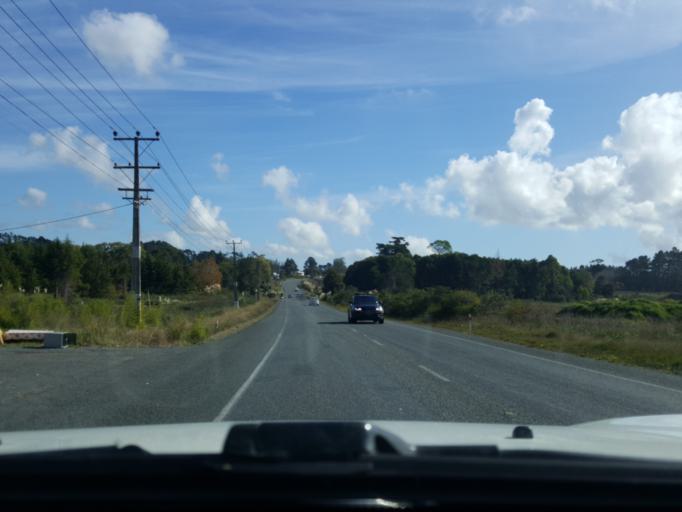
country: NZ
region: Auckland
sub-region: Auckland
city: Muriwai Beach
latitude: -36.7692
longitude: 174.5303
